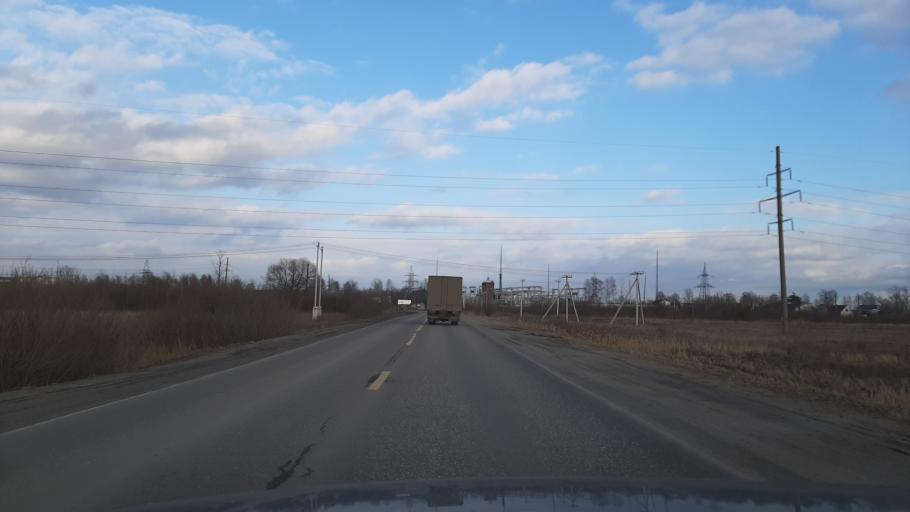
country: RU
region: Ivanovo
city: Novo-Talitsy
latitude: 56.9877
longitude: 40.9020
